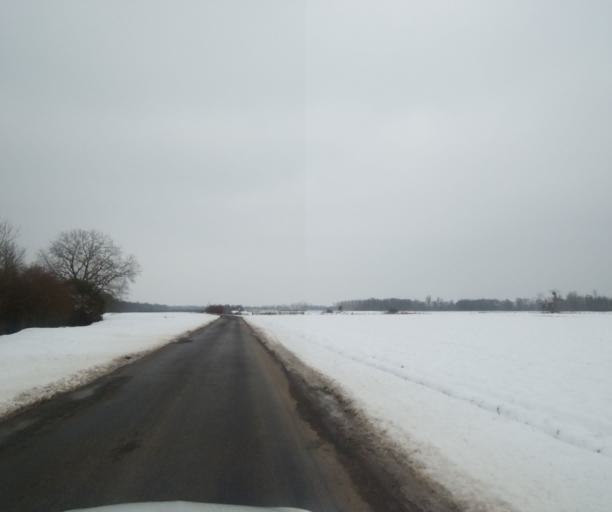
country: FR
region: Champagne-Ardenne
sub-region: Departement de la Haute-Marne
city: Wassy
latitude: 48.5653
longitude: 4.8945
